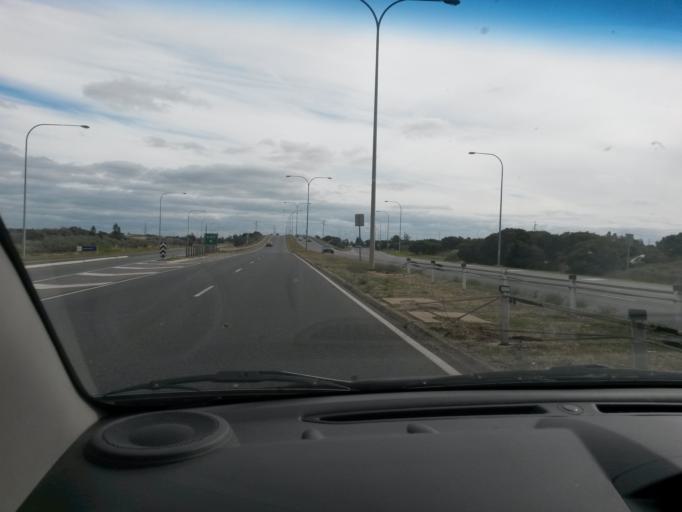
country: AU
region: South Australia
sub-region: Salisbury
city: Ingle Farm
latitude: -34.8083
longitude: 138.6004
